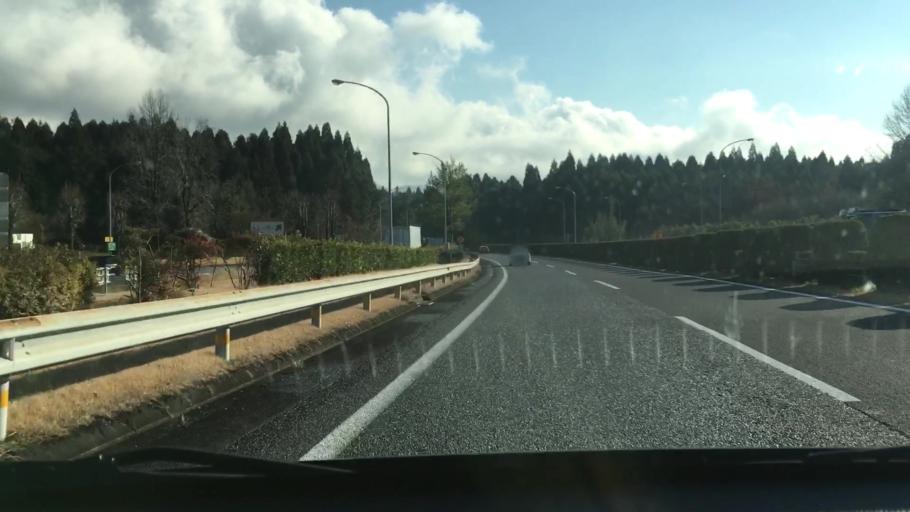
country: JP
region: Kagoshima
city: Okuchi-shinohara
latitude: 32.0065
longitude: 130.7556
